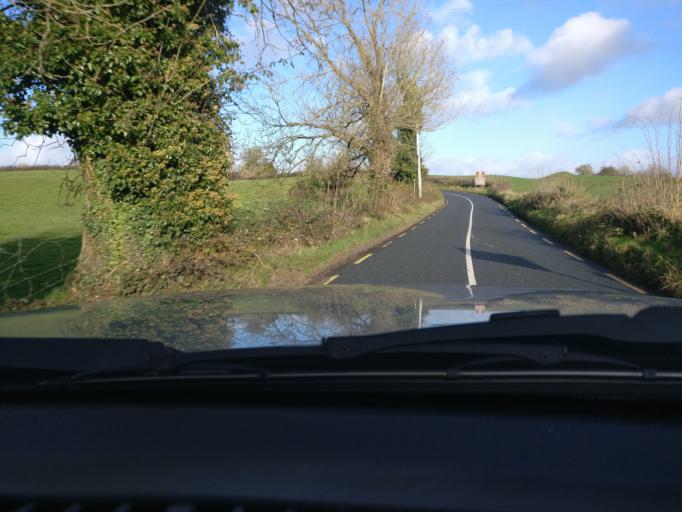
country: IE
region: Leinster
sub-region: Uibh Fhaili
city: Clara
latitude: 53.3949
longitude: -7.5829
